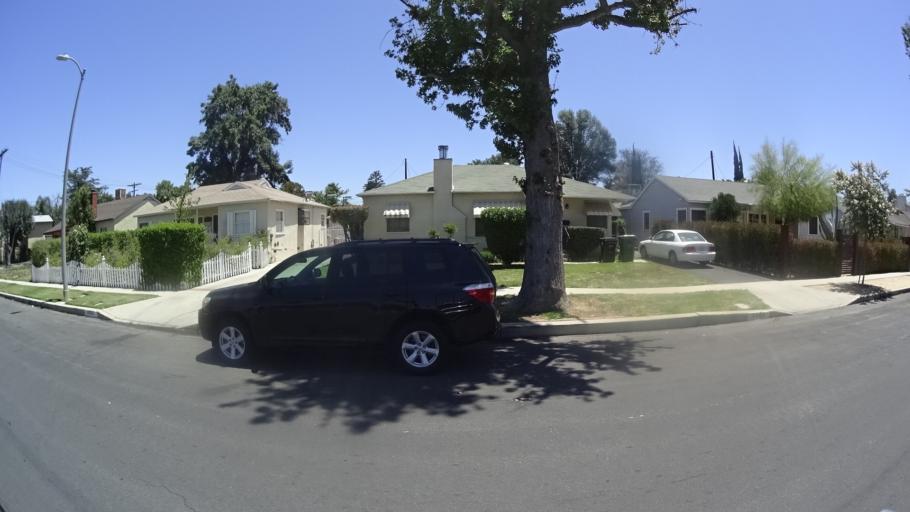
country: US
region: California
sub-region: Los Angeles County
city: Northridge
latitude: 34.1972
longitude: -118.5142
